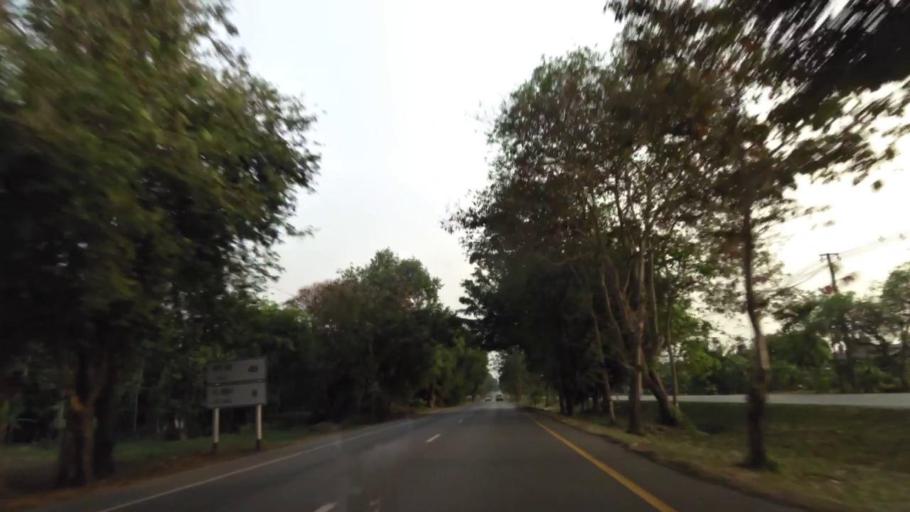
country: TH
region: Chanthaburi
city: Khlung
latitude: 12.4944
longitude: 102.1729
